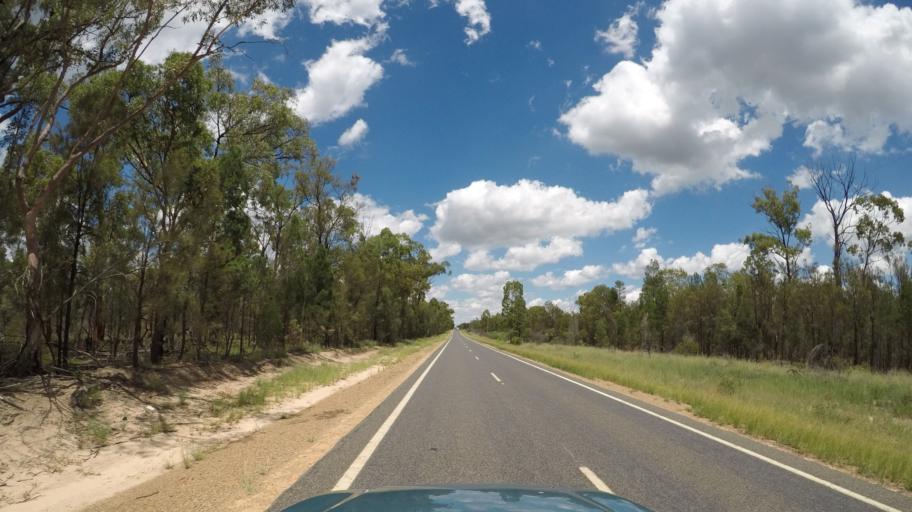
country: AU
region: New South Wales
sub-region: Moree Plains
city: Boggabilla
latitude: -27.9901
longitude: 150.9608
